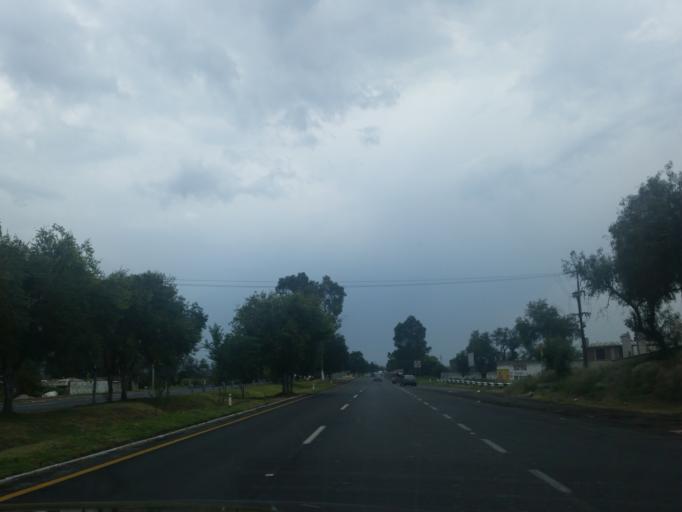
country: MX
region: Morelos
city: Teotihuacan de Arista
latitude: 19.6790
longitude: -98.8605
